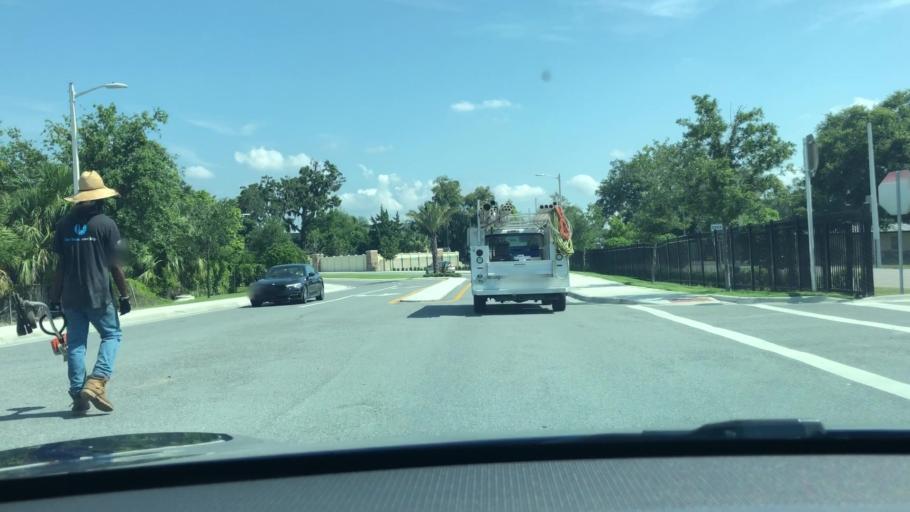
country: US
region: Florida
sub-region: Orange County
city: Eatonville
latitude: 28.6048
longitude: -81.3629
